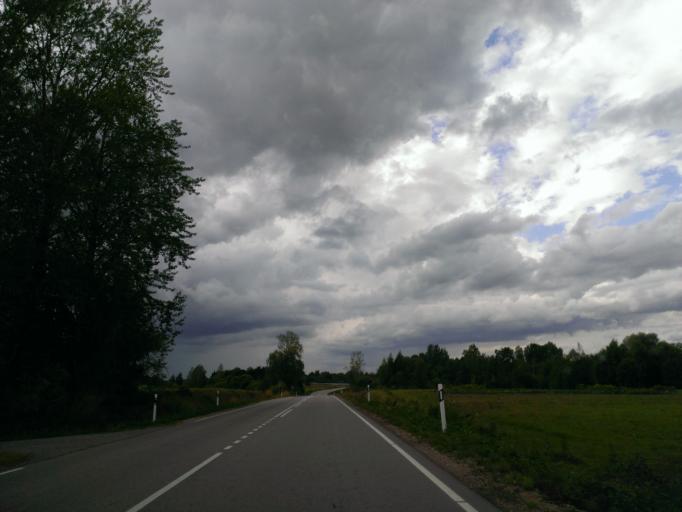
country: LV
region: Malpils
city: Malpils
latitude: 56.8965
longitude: 25.1357
